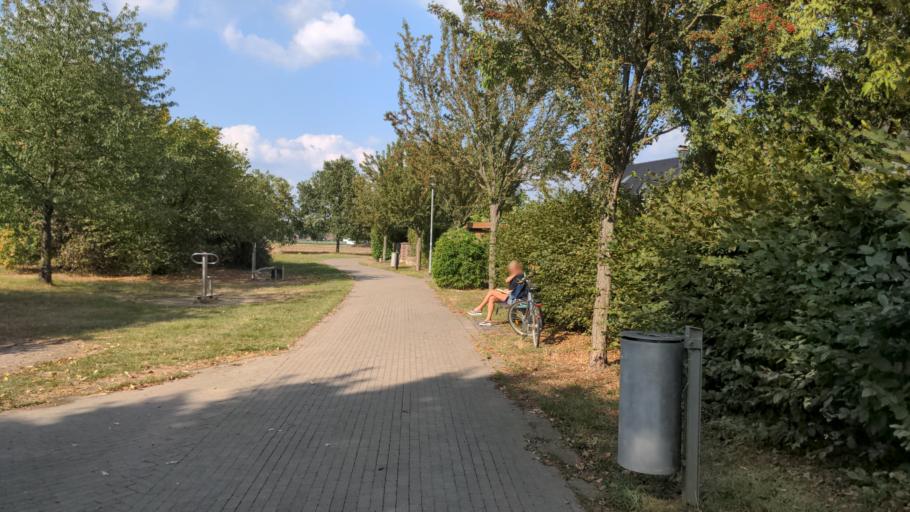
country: DE
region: North Rhine-Westphalia
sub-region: Regierungsbezirk Dusseldorf
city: Kaarst
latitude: 51.2158
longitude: 6.5815
